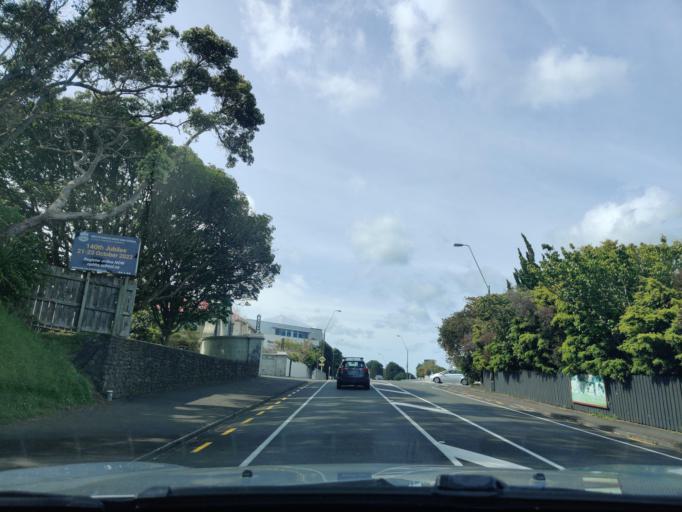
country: NZ
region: Taranaki
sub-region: New Plymouth District
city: New Plymouth
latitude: -39.0603
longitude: 174.0853
